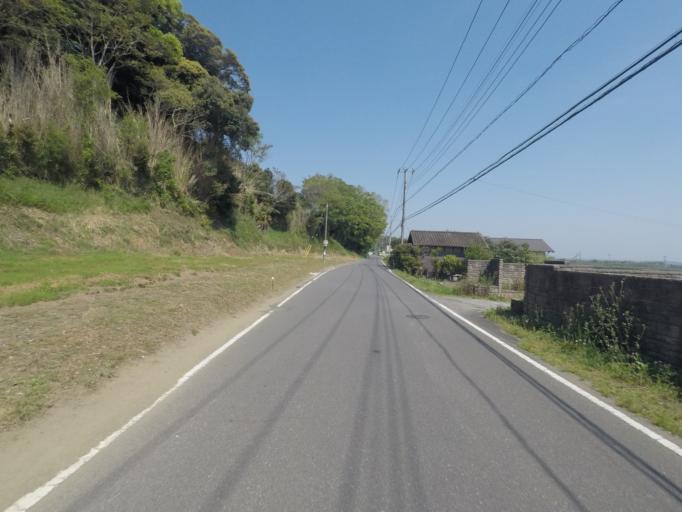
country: JP
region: Ibaraki
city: Ami
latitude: 36.0731
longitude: 140.2707
